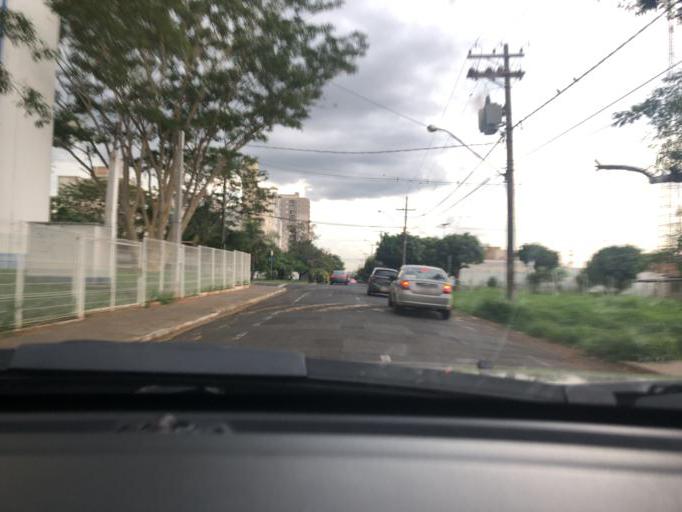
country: BR
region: Sao Paulo
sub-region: Sao Jose Do Rio Preto
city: Sao Jose do Rio Preto
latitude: -20.8410
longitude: -49.3841
